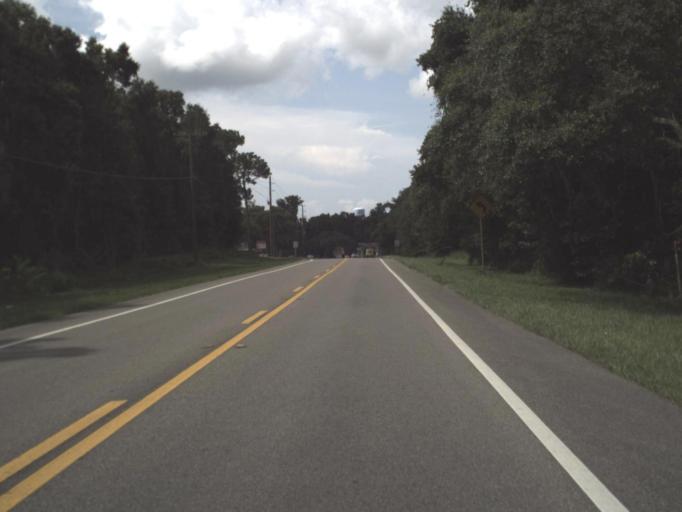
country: US
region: Florida
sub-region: Citrus County
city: Floral City
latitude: 28.7737
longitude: -82.2941
